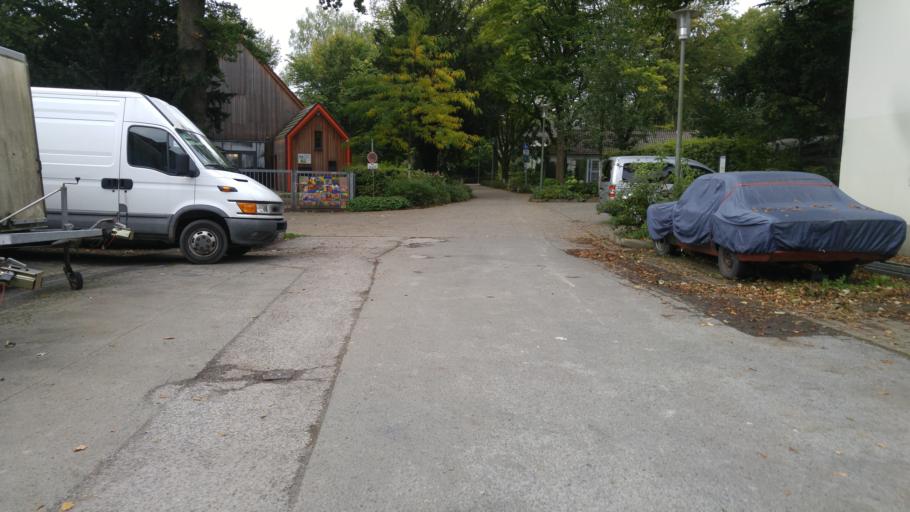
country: DE
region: North Rhine-Westphalia
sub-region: Regierungsbezirk Detmold
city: Bielefeld
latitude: 52.0392
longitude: 8.5295
